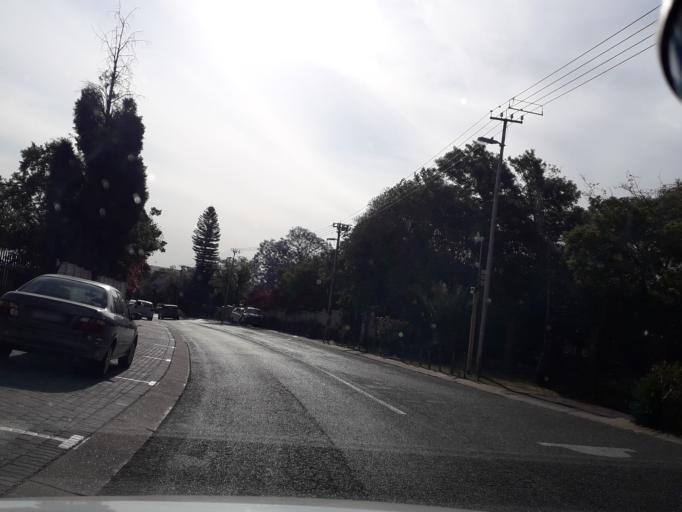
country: ZA
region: Gauteng
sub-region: City of Johannesburg Metropolitan Municipality
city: Diepsloot
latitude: -26.0494
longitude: 28.0064
